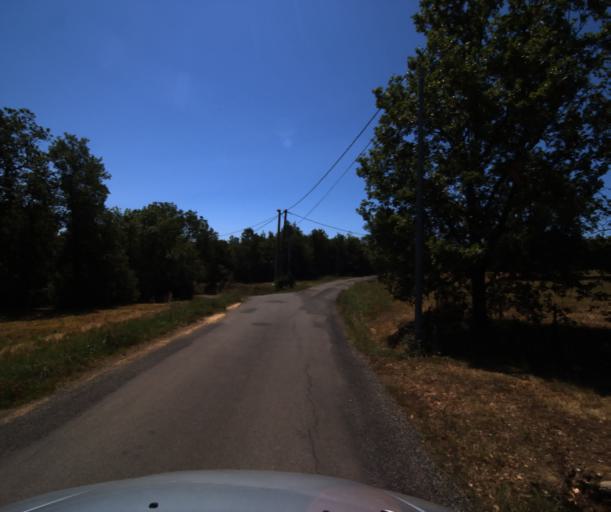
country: FR
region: Midi-Pyrenees
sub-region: Departement de la Haute-Garonne
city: Muret
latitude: 43.4555
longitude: 1.3441
